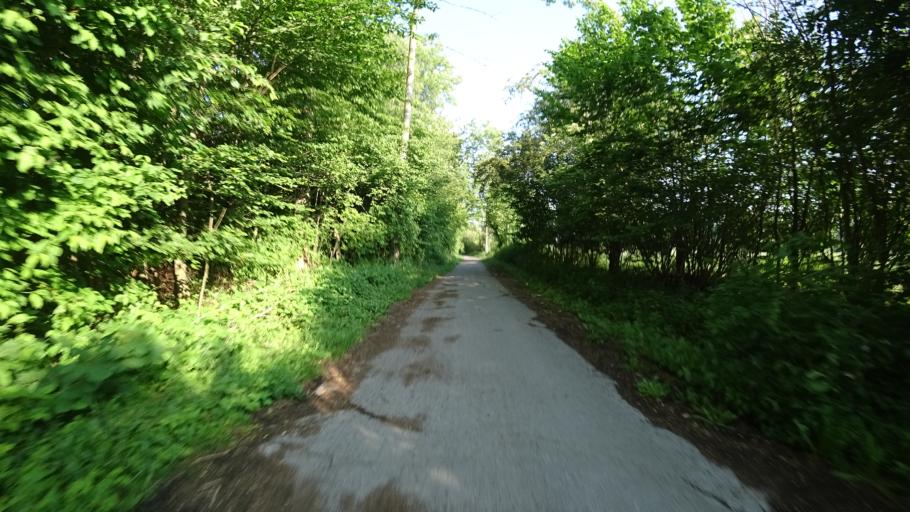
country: DE
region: North Rhine-Westphalia
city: Erwitte
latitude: 51.6360
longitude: 8.3840
